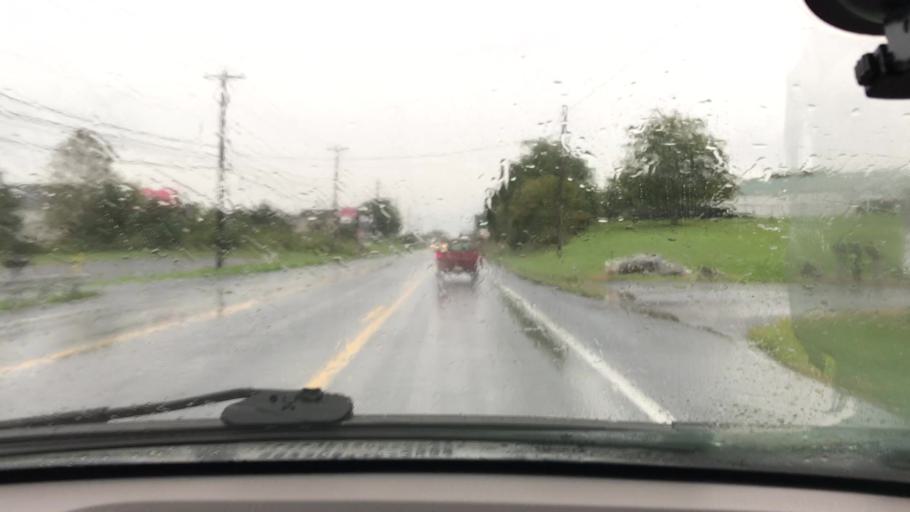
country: US
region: Pennsylvania
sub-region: Lancaster County
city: Rheems
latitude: 40.1339
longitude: -76.5720
